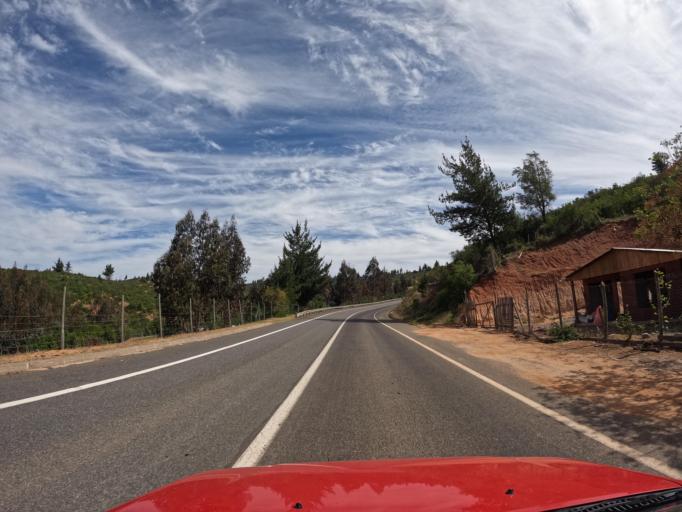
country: CL
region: Maule
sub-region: Provincia de Talca
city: Talca
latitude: -35.1561
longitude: -71.9616
